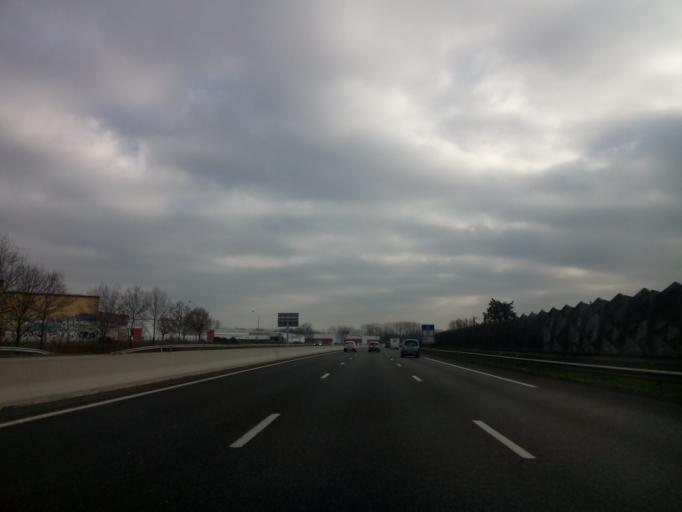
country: FR
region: Rhone-Alpes
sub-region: Departement de l'Isere
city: La Verpilliere
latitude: 45.6452
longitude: 5.1358
